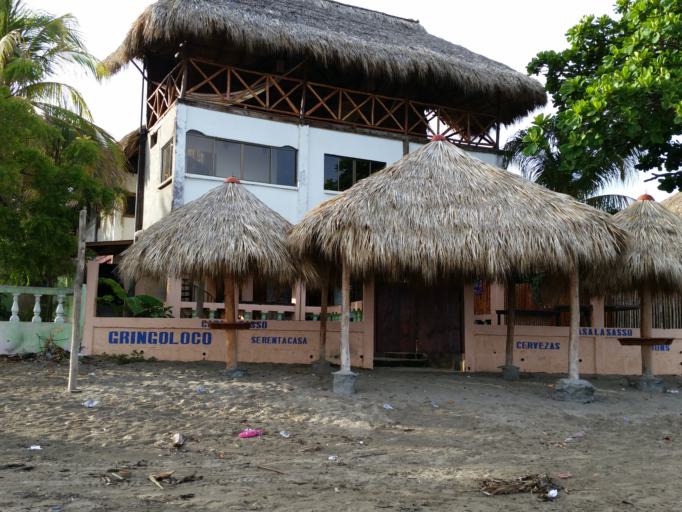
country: NI
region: Managua
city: Masachapa
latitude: 11.7820
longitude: -86.5186
